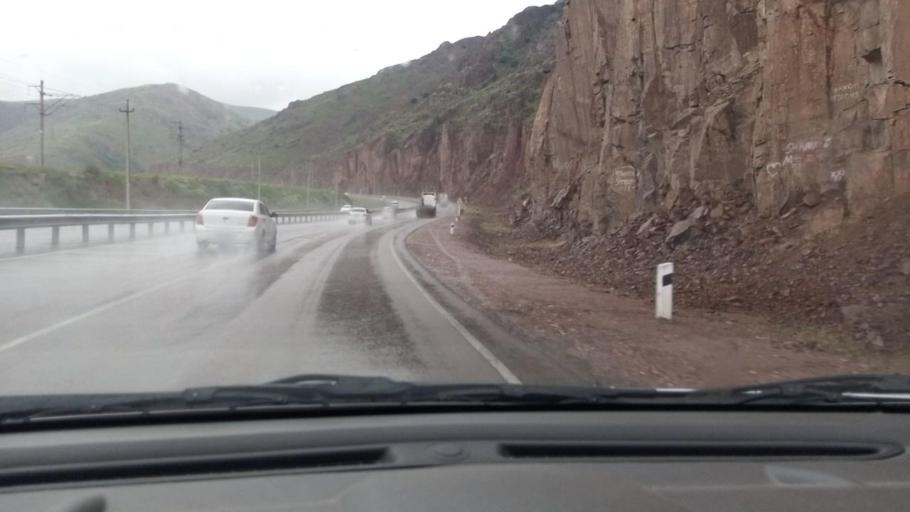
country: UZ
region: Toshkent
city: Angren
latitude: 41.0744
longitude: 70.3089
